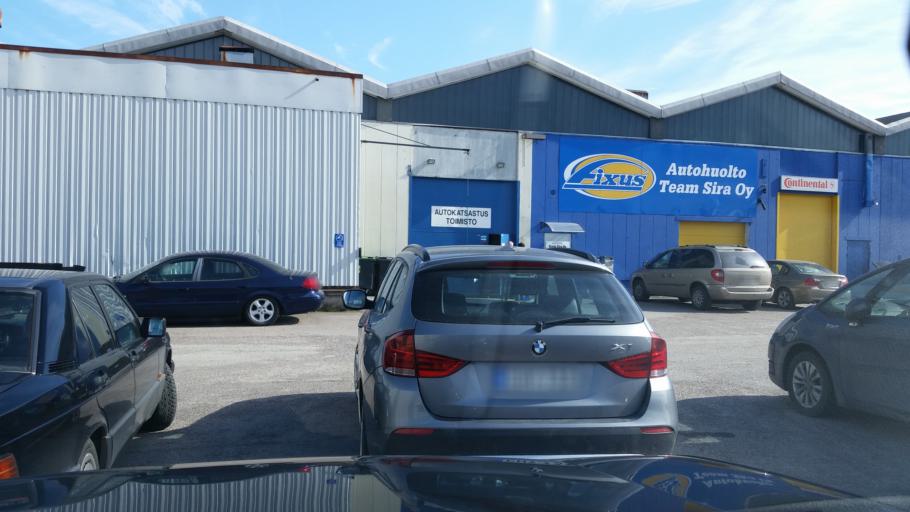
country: FI
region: Uusimaa
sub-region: Helsinki
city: Helsinki
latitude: 60.1500
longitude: 24.9234
